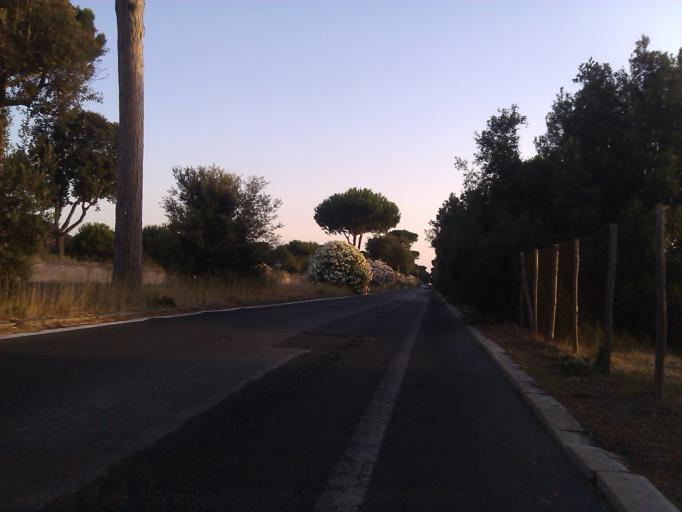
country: IT
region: Latium
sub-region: Citta metropolitana di Roma Capitale
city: Acilia-Castel Fusano-Ostia Antica
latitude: 41.7256
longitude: 12.3313
